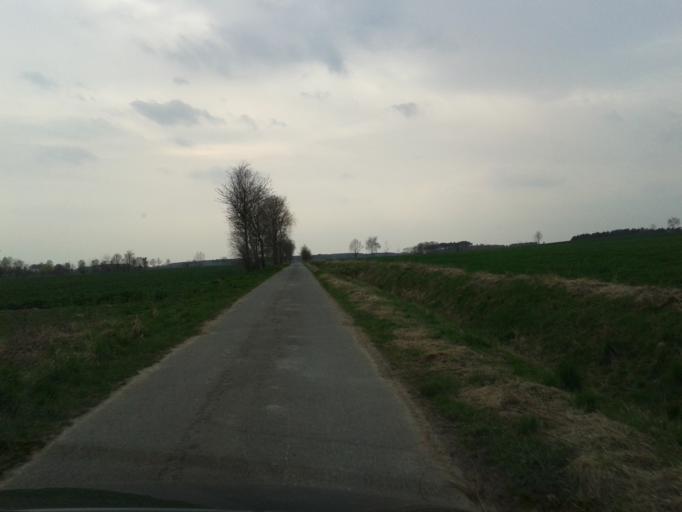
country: DE
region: Lower Saxony
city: Woltersdorf
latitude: 52.9215
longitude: 11.2604
